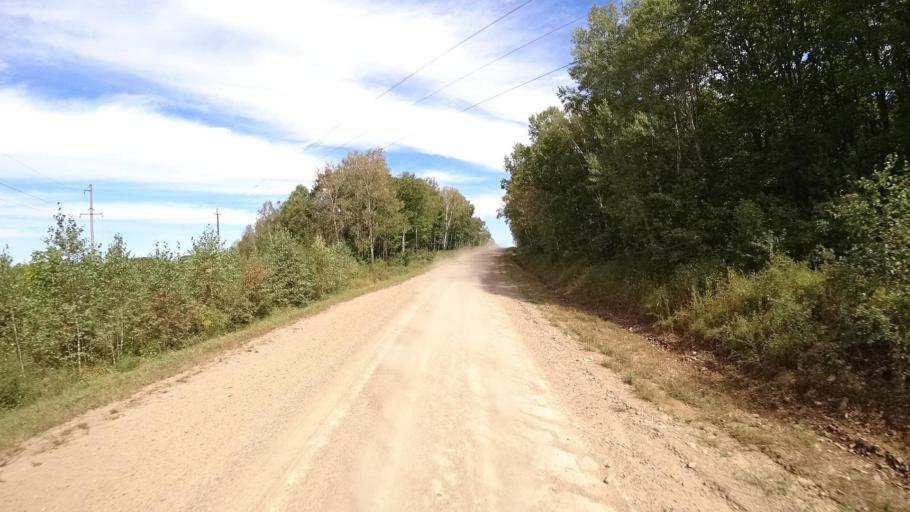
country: RU
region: Primorskiy
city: Yakovlevka
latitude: 44.6960
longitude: 133.6209
